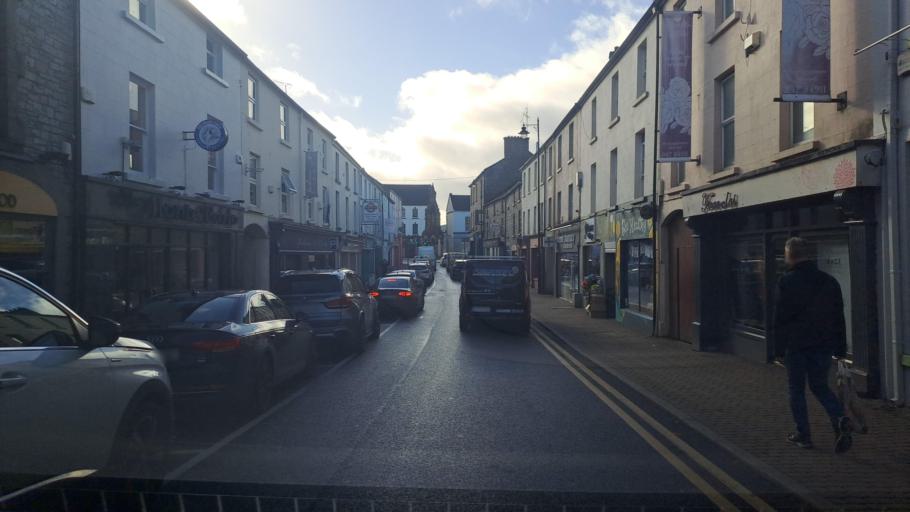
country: IE
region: Ulster
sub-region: County Monaghan
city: Monaghan
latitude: 54.2495
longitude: -6.9682
